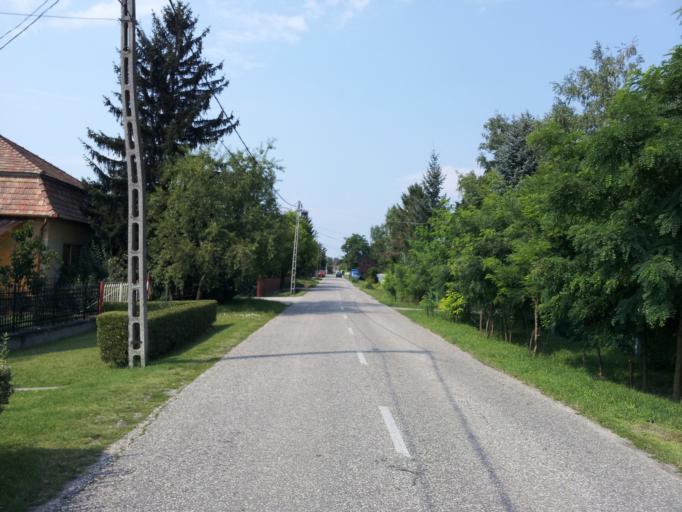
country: HU
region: Pest
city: Szigetujfalu
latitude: 47.2271
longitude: 18.9207
